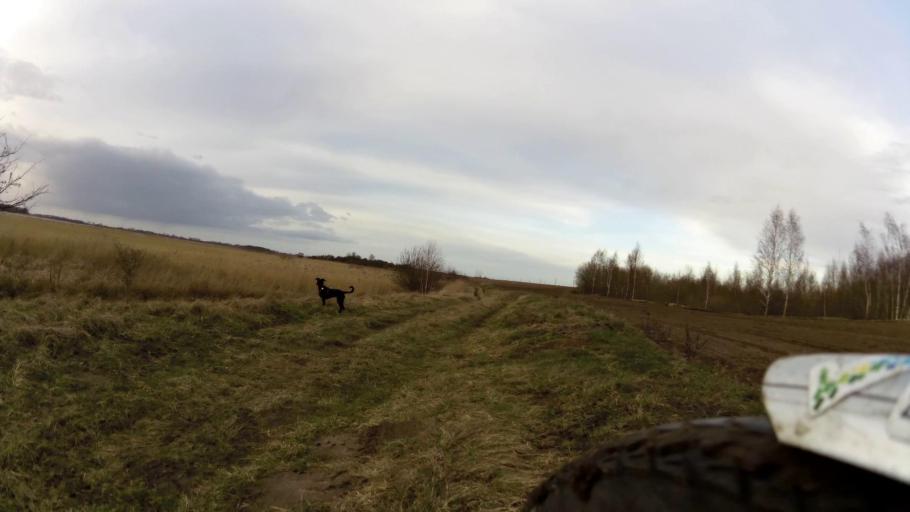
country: PL
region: West Pomeranian Voivodeship
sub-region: Powiat kamienski
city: Kamien Pomorski
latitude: 53.9274
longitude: 14.7620
